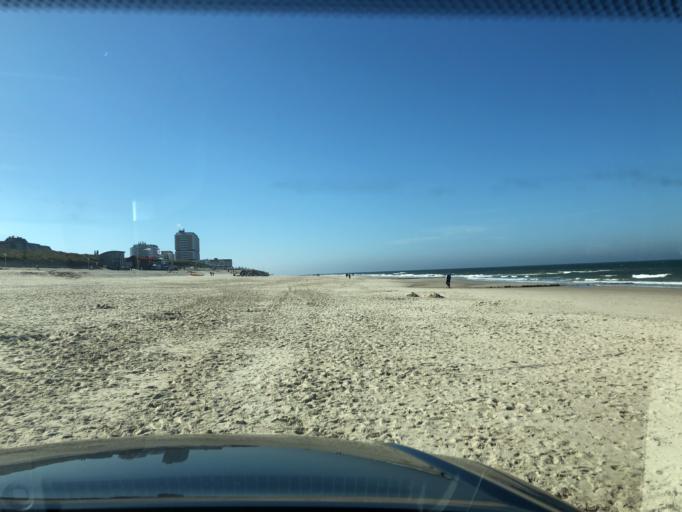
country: DE
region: Schleswig-Holstein
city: Westerland
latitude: 54.9146
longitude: 8.3008
